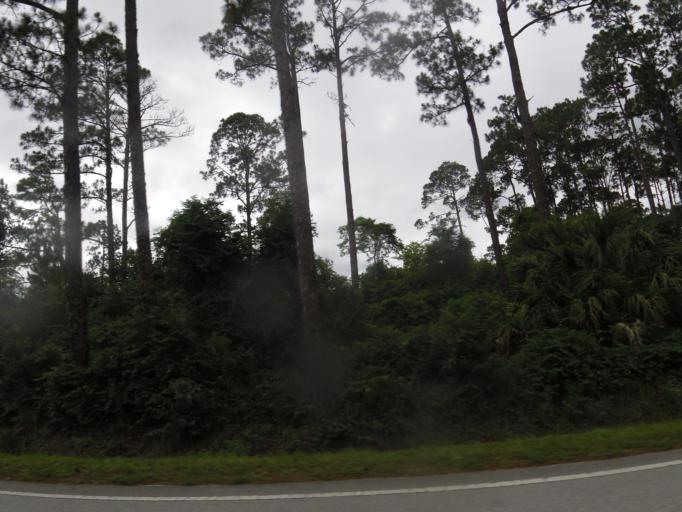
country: US
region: Florida
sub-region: Saint Johns County
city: Saint Augustine
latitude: 29.8818
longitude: -81.3615
